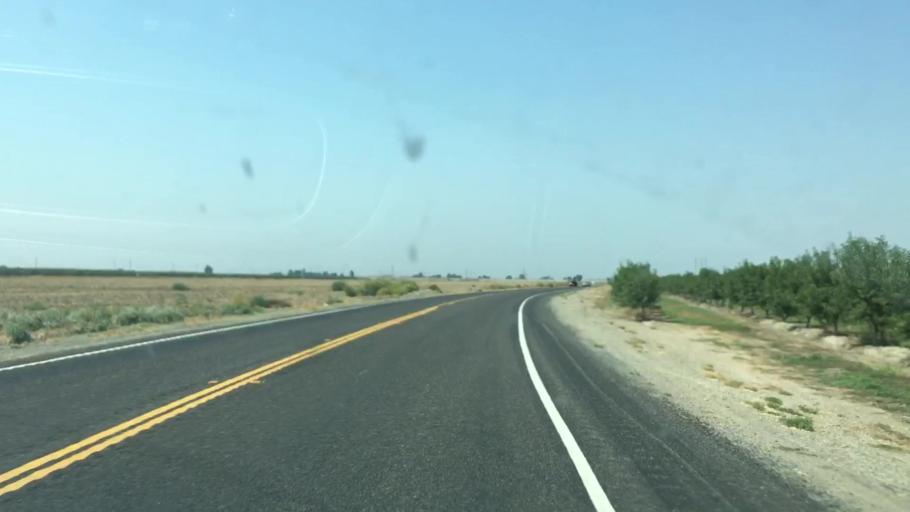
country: US
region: California
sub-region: San Joaquin County
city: French Camp
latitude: 37.8774
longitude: -121.3065
